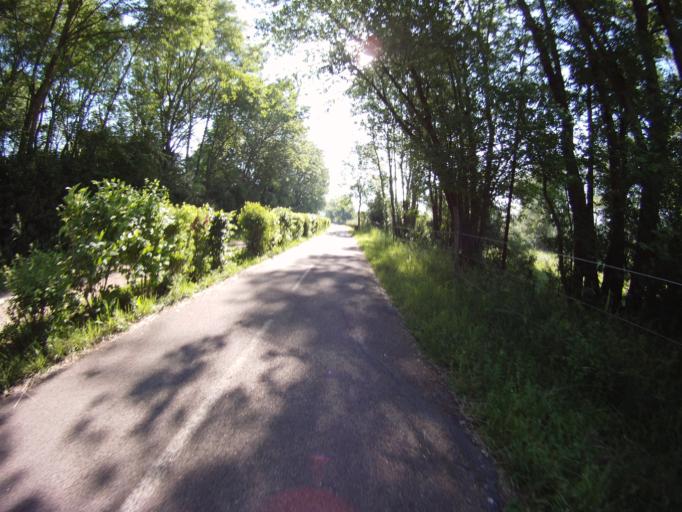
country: FR
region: Lorraine
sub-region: Departement de Meurthe-et-Moselle
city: Eulmont
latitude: 48.7406
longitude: 6.2349
